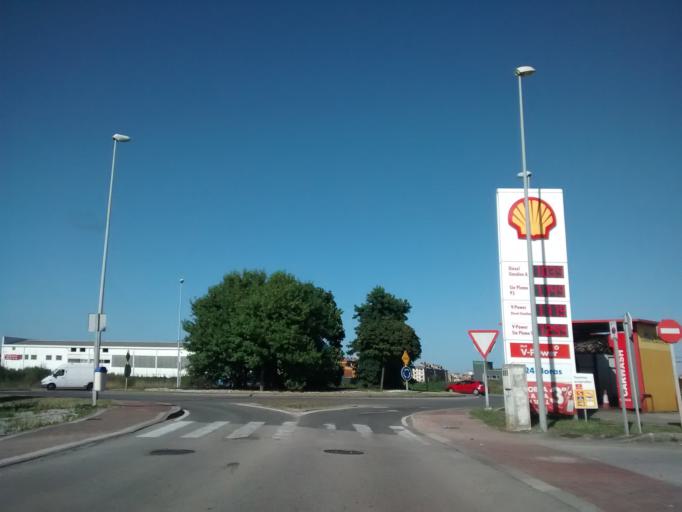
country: ES
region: Cantabria
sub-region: Provincia de Cantabria
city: Santander
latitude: 43.4646
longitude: -3.8337
